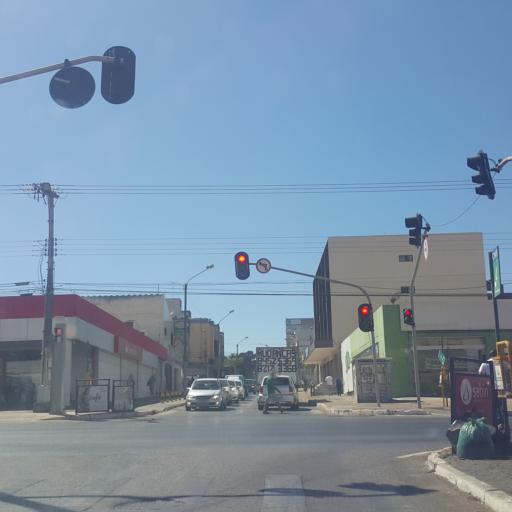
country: BR
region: Federal District
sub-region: Brasilia
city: Brasilia
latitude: -15.8281
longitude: -48.0592
